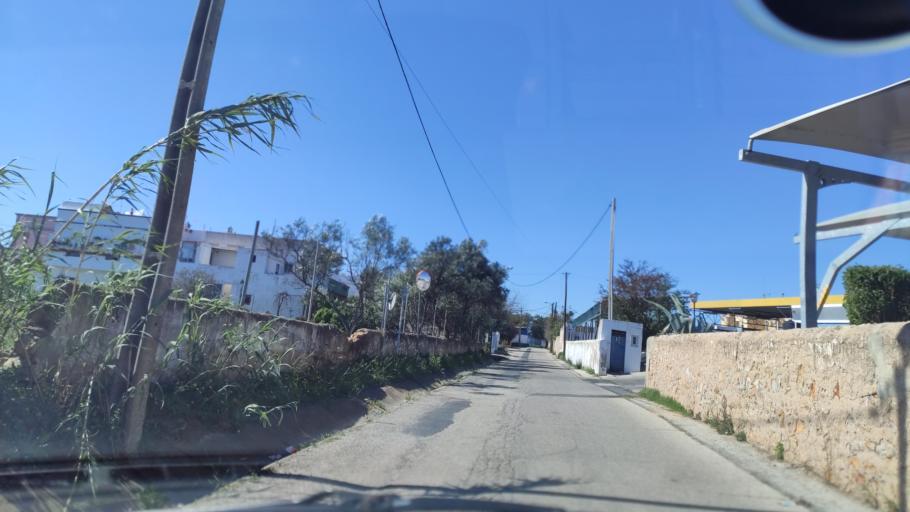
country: PT
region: Faro
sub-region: Olhao
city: Olhao
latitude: 37.0293
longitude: -7.8535
